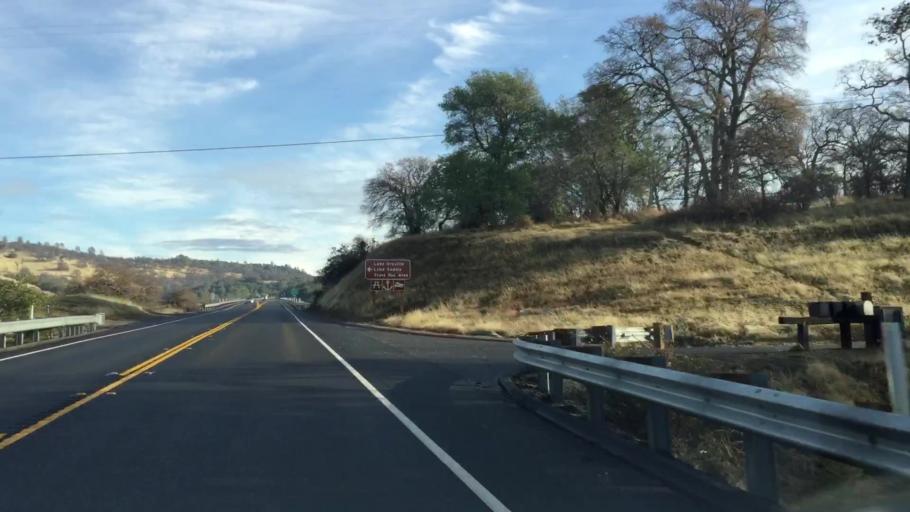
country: US
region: California
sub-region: Butte County
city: Paradise
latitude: 39.6479
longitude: -121.5627
